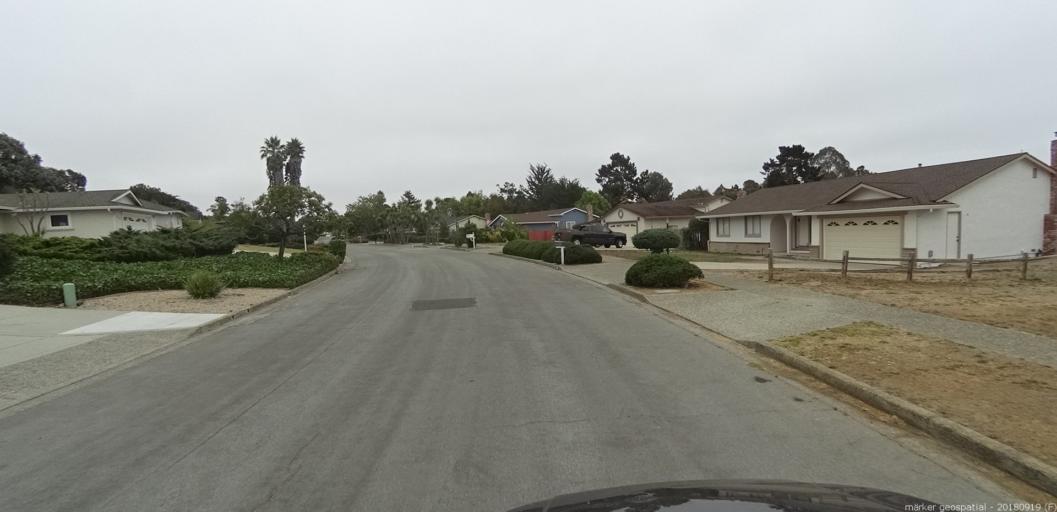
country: US
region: California
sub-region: Monterey County
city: Castroville
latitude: 36.7776
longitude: -121.7245
